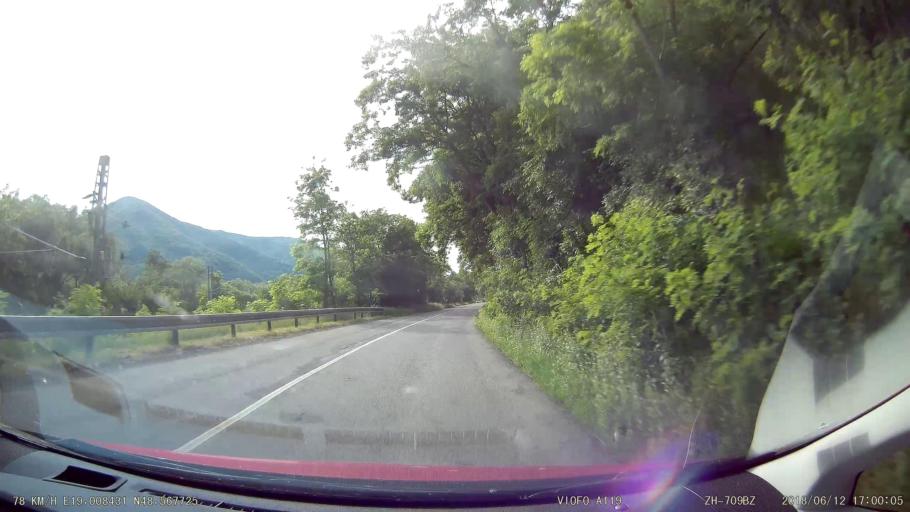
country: SK
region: Banskobystricky
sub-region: Okres Banska Bystrica
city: Zvolen
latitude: 48.5678
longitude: 19.0082
